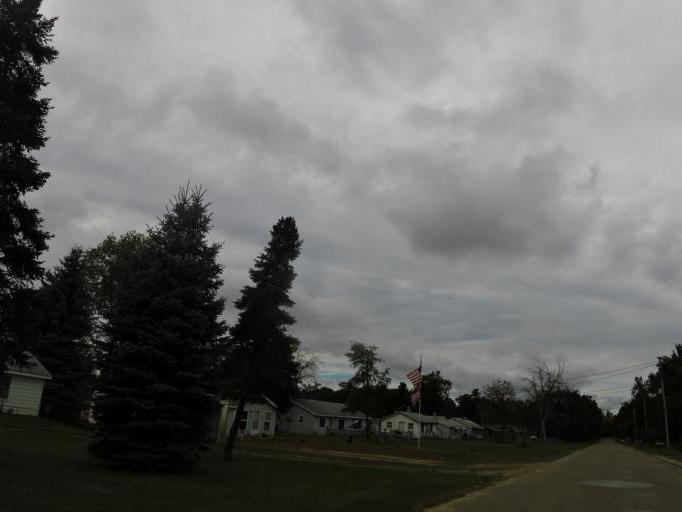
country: US
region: Michigan
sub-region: Roscommon County
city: Saint Helen
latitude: 44.3493
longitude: -84.4338
